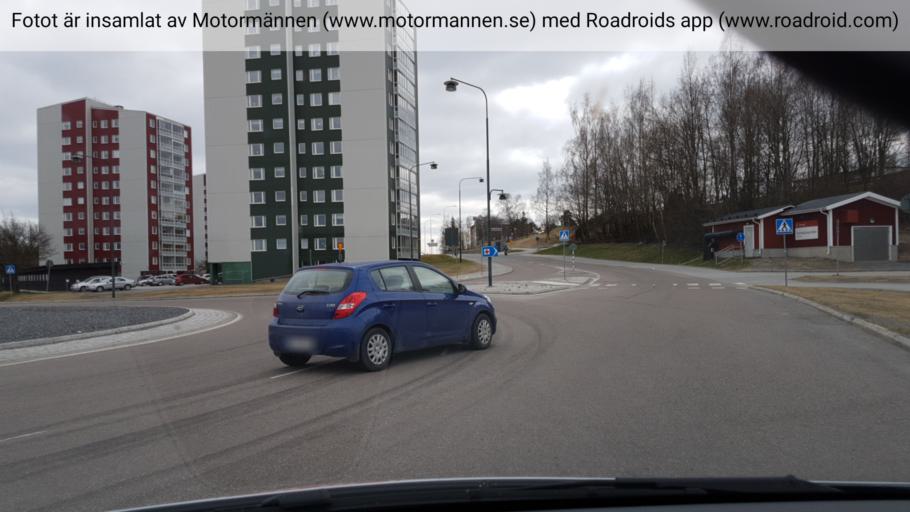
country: SE
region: Vaesternorrland
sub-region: OErnskoeldsviks Kommun
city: Ornskoldsvik
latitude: 63.3020
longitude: 18.7159
